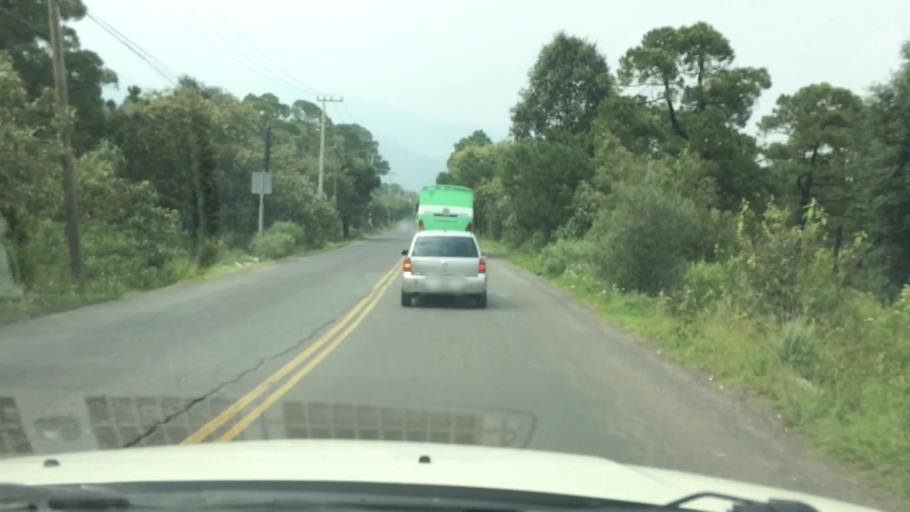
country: MX
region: Mexico City
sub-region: Tlalpan
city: Lomas de Tepemecatl
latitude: 19.2610
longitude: -99.2376
